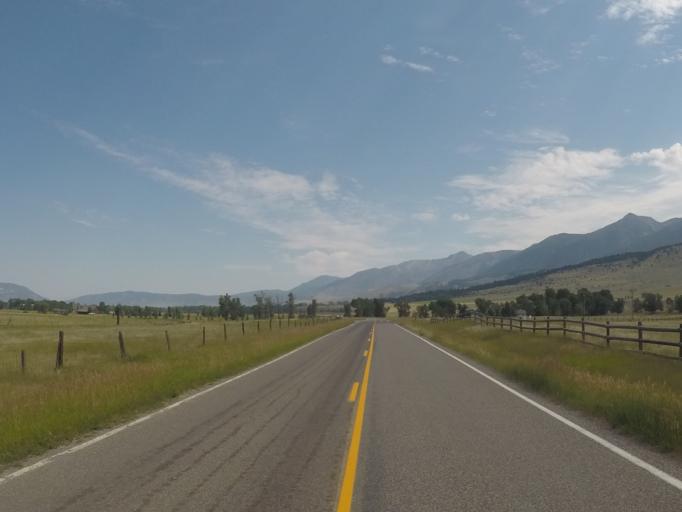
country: US
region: Montana
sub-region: Park County
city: Livingston
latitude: 45.4308
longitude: -110.6158
